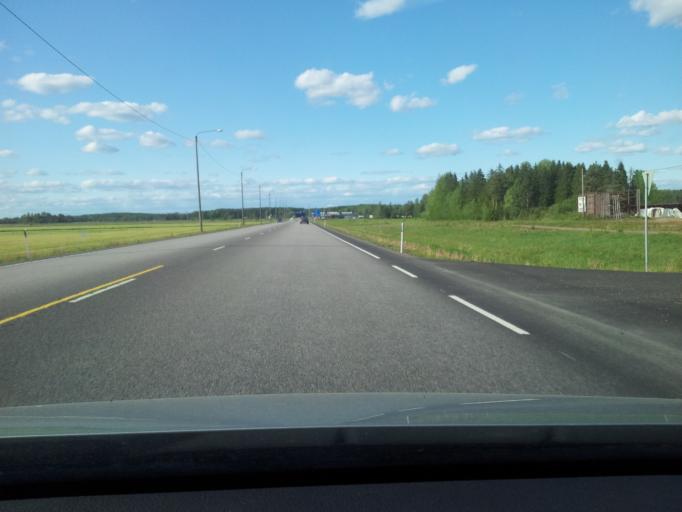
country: FI
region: Uusimaa
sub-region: Loviisa
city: Lapinjaervi
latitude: 60.6647
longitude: 26.2469
